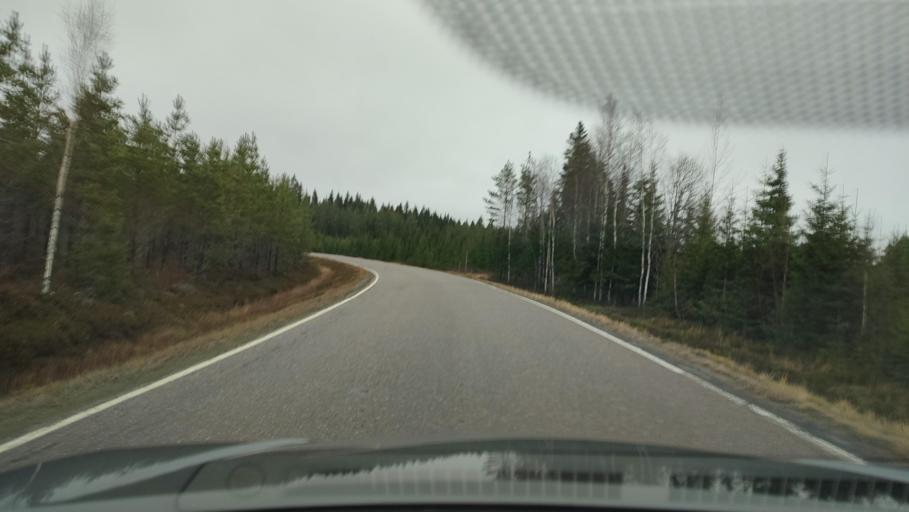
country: FI
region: Southern Ostrobothnia
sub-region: Suupohja
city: Isojoki
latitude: 62.2217
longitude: 22.0001
